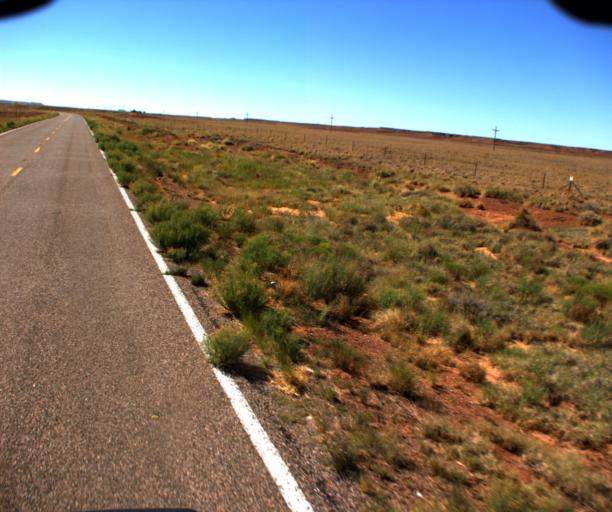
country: US
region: Arizona
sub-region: Coconino County
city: LeChee
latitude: 35.1654
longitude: -110.9134
